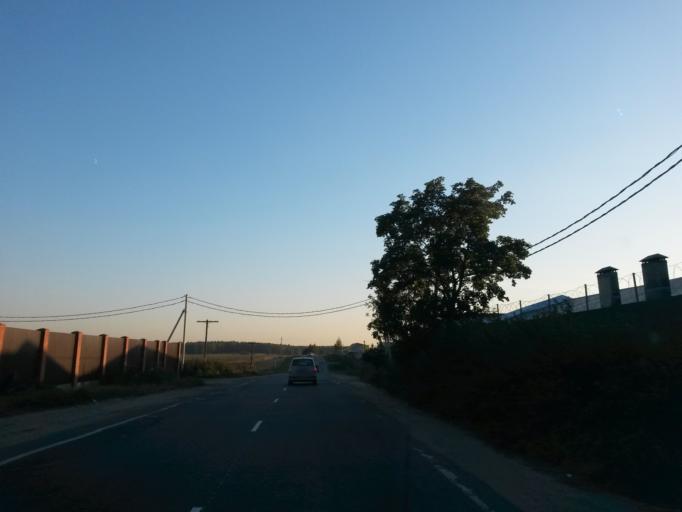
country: RU
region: Moskovskaya
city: Vostryakovo
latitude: 55.3533
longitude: 37.7429
